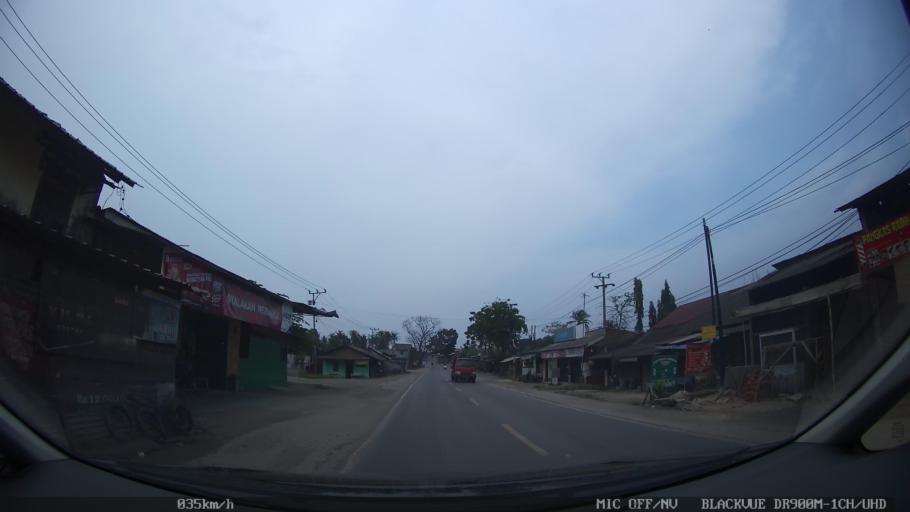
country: ID
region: Lampung
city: Panjang
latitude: -5.4294
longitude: 105.3271
